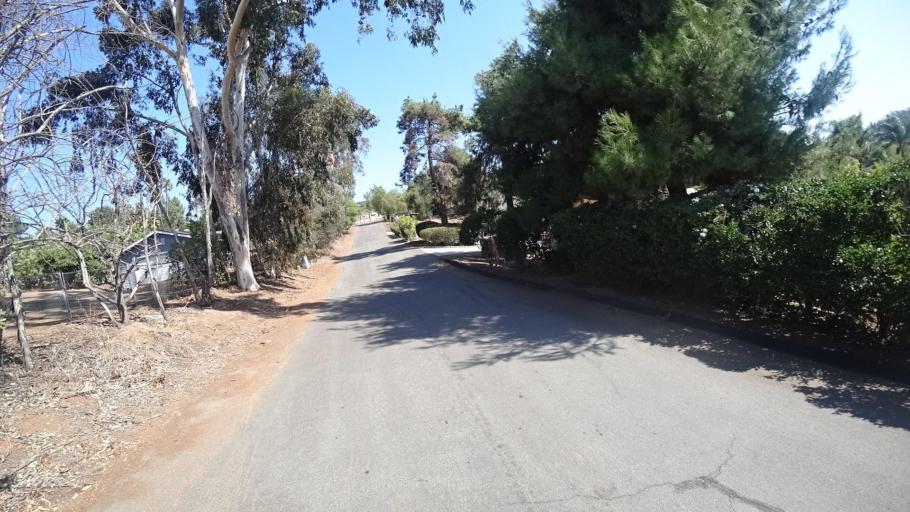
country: US
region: California
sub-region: San Diego County
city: Granite Hills
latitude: 32.7840
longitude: -116.8984
